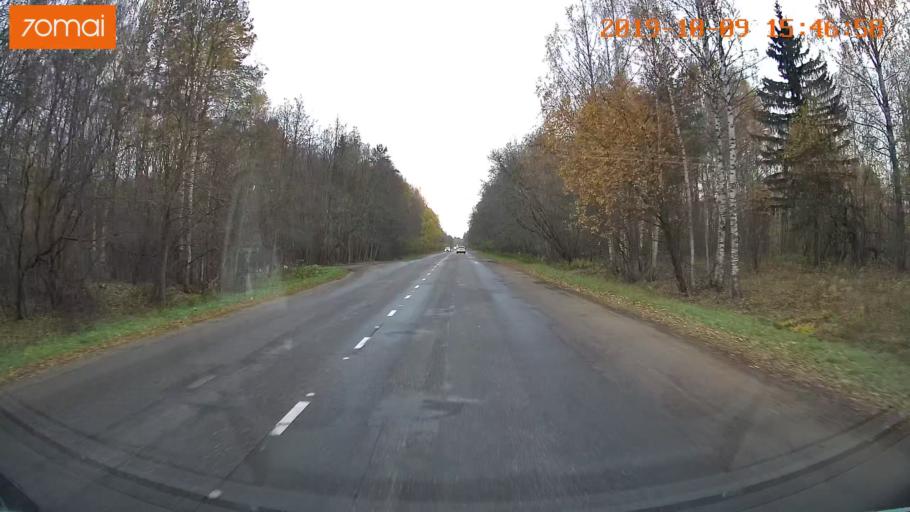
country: RU
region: Kostroma
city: Oktyabr'skiy
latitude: 57.8207
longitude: 41.0356
